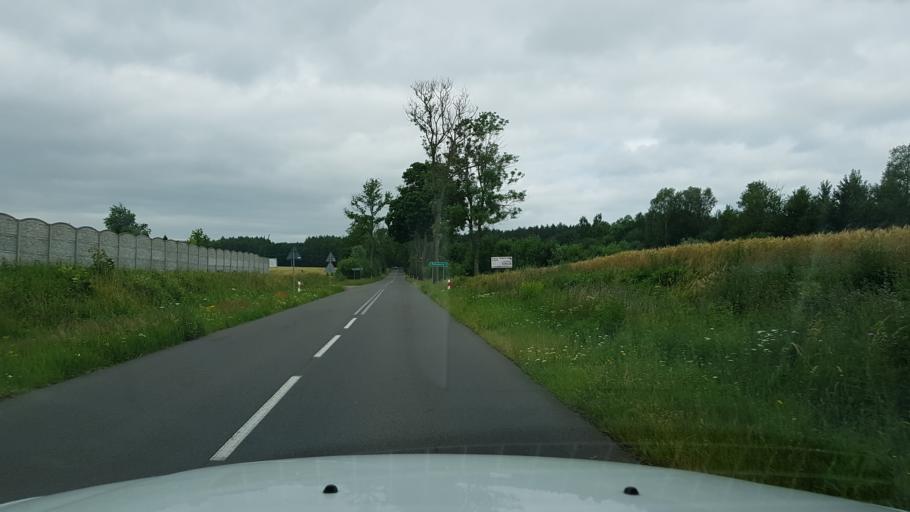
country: PL
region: West Pomeranian Voivodeship
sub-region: Powiat gryficki
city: Cerkwica
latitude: 53.9259
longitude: 15.1025
